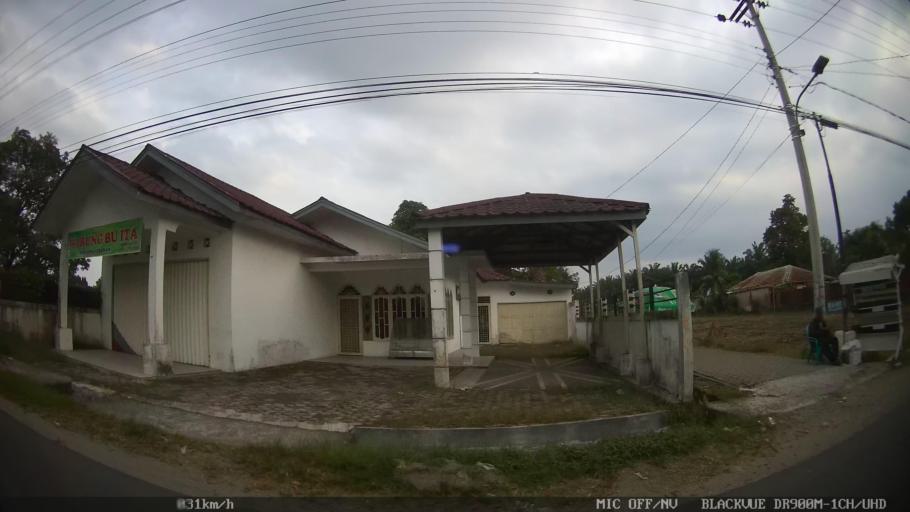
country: ID
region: North Sumatra
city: Sunggal
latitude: 3.5595
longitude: 98.5583
